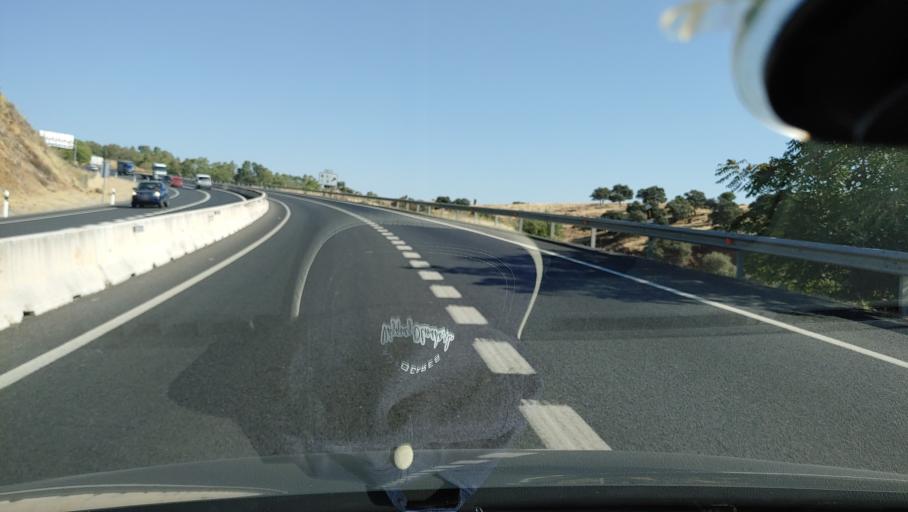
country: ES
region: Andalusia
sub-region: Province of Cordoba
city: Cordoba
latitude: 37.9103
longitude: -4.7528
